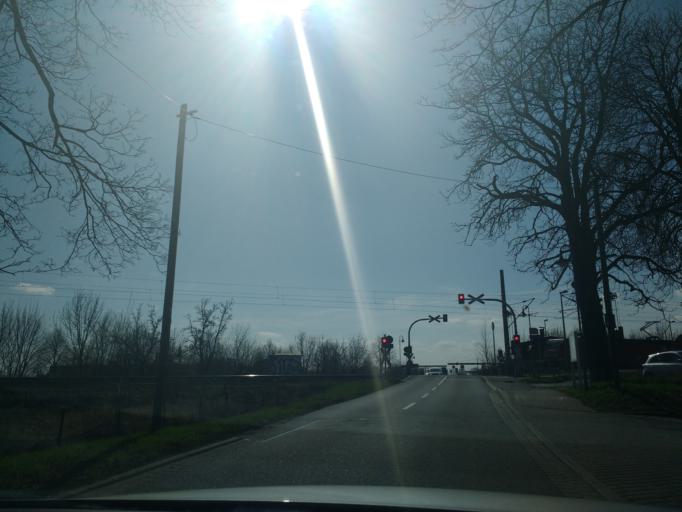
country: DE
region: Saxony-Anhalt
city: Peissen
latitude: 51.5052
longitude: 12.0338
